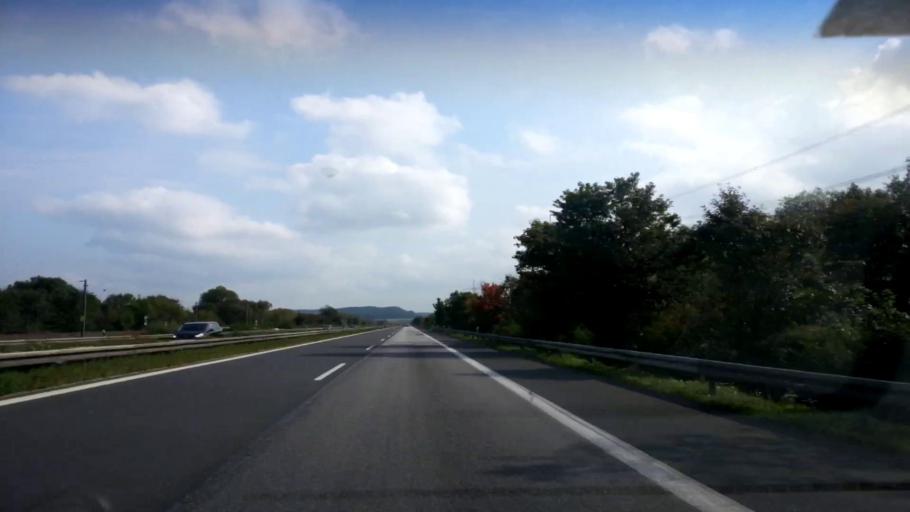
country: DE
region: Bavaria
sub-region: Regierungsbezirk Unterfranken
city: Ebelsbach
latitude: 49.9737
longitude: 10.6968
